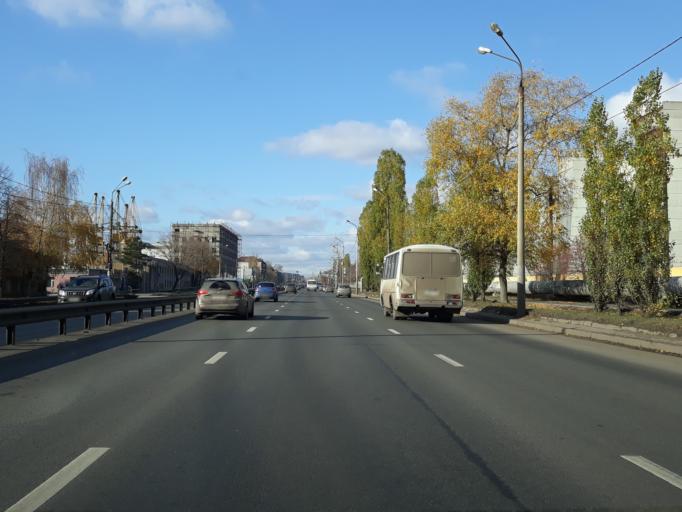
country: RU
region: Nizjnij Novgorod
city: Nizhniy Novgorod
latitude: 56.2626
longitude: 43.9247
